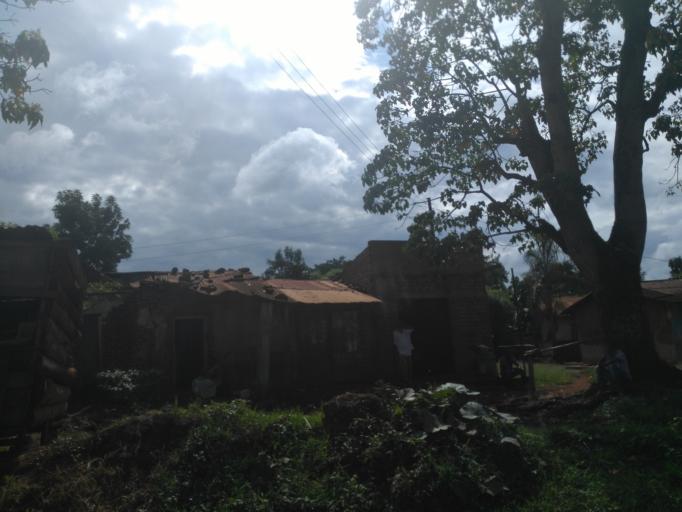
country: UG
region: Central Region
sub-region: Buikwe District
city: Njeru
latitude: 0.4023
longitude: 33.1770
